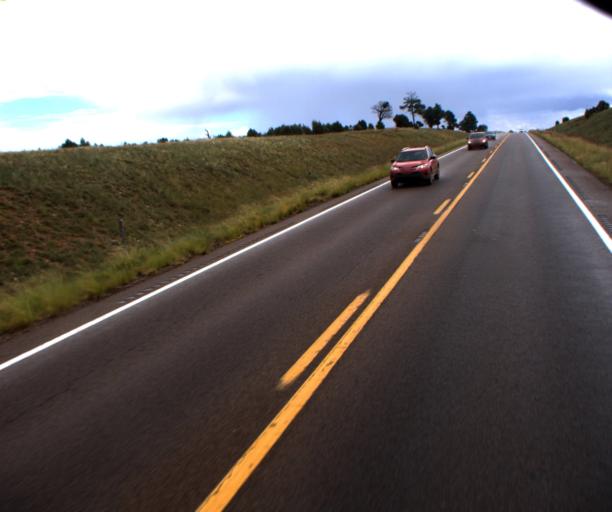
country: US
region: Arizona
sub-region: Navajo County
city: Heber-Overgaard
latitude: 34.3810
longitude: -110.4797
